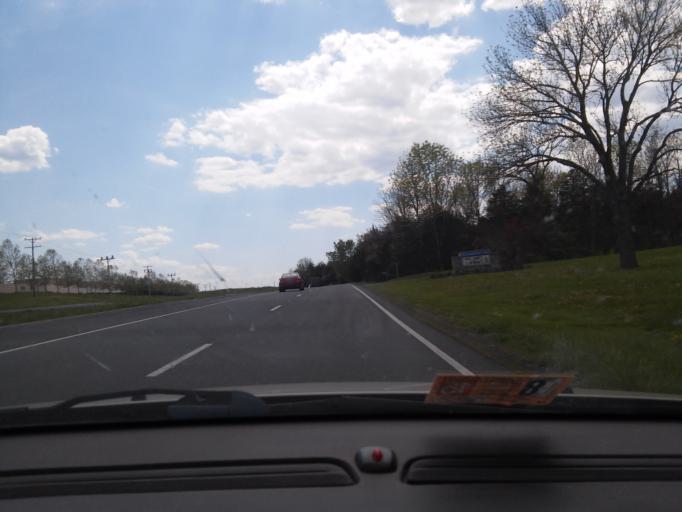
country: US
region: Virginia
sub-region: Frederick County
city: Stephens City
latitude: 39.0124
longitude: -78.1666
